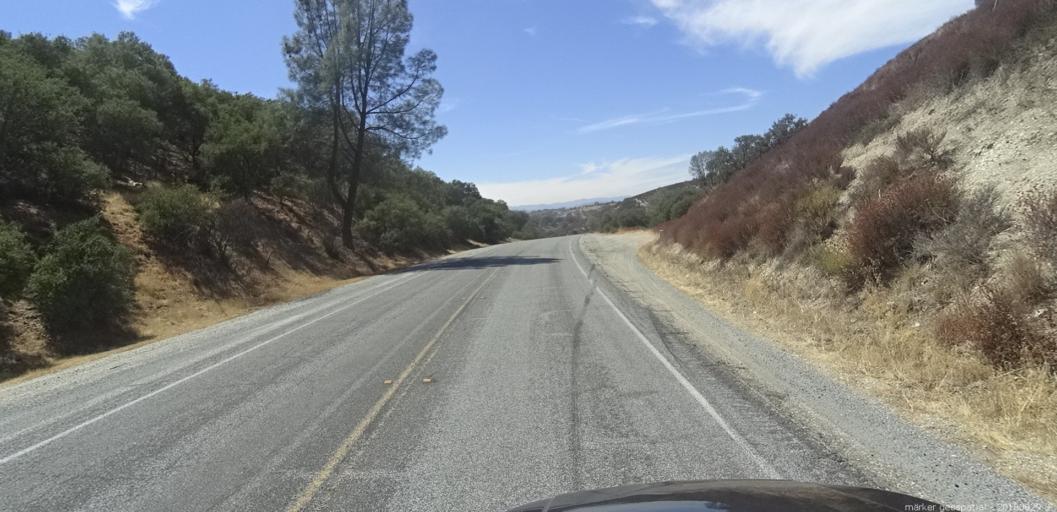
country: US
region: California
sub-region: San Luis Obispo County
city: Lake Nacimiento
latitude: 35.9036
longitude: -120.9687
